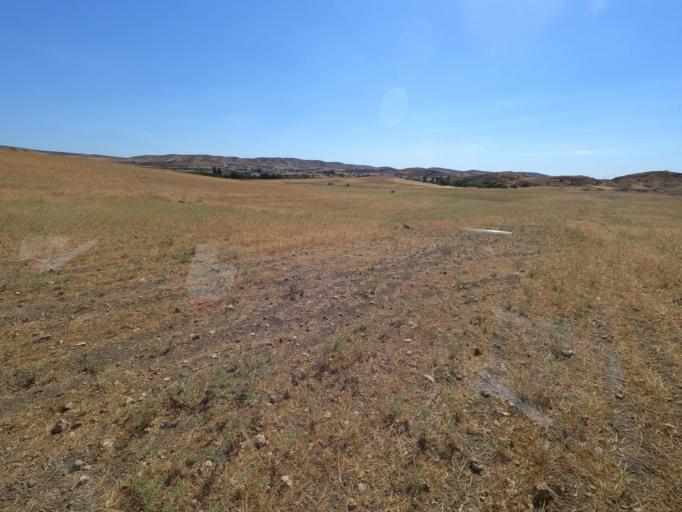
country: CY
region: Larnaka
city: Troulloi
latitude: 35.0242
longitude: 33.5981
